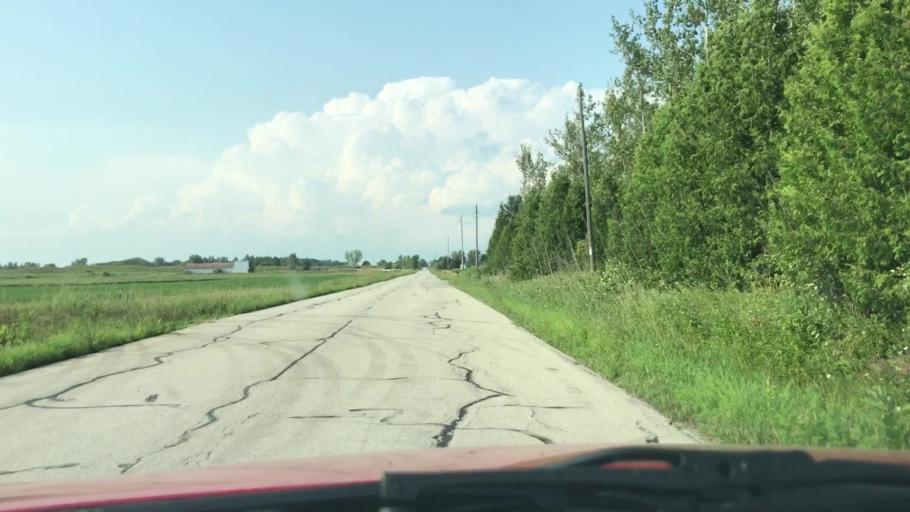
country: US
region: Wisconsin
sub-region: Brown County
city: Oneida
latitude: 44.4336
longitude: -88.1705
